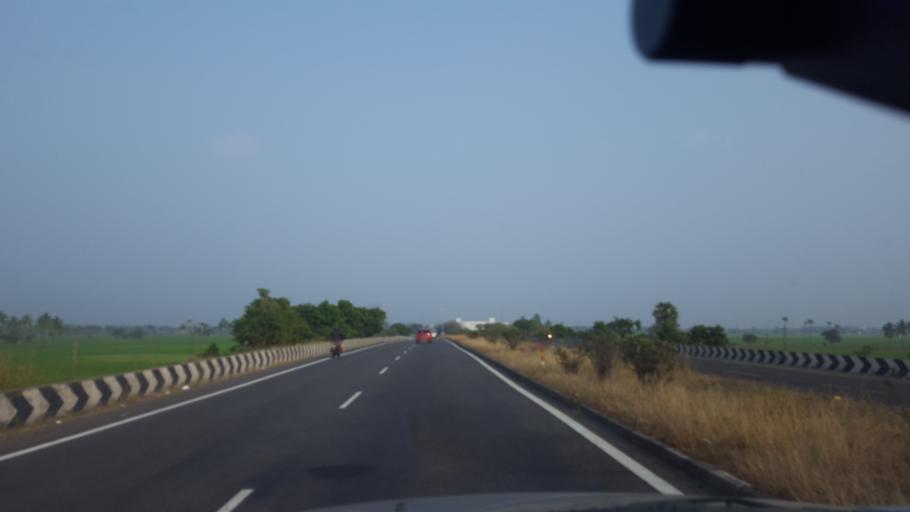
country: IN
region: Andhra Pradesh
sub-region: West Godavari
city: Tadepallegudem
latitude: 16.8344
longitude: 81.4887
